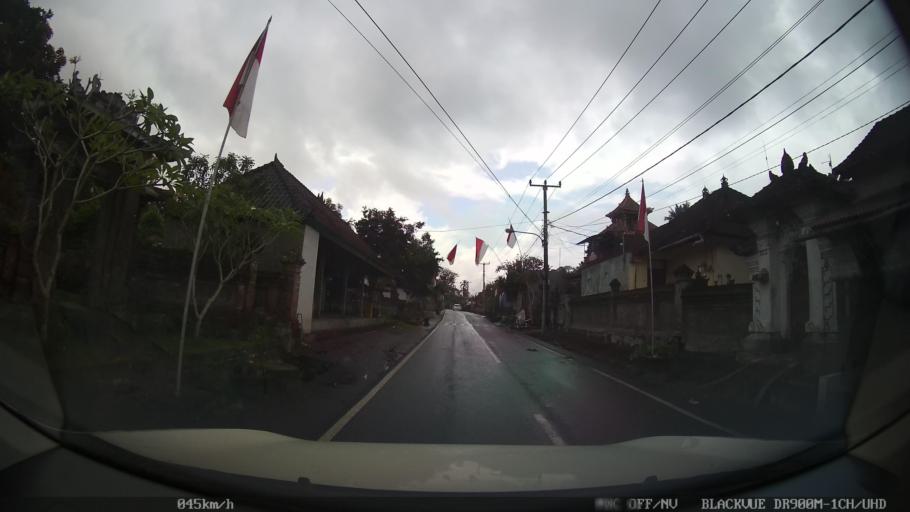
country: ID
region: Bali
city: Banjar Teguan
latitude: -8.5190
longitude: 115.2289
